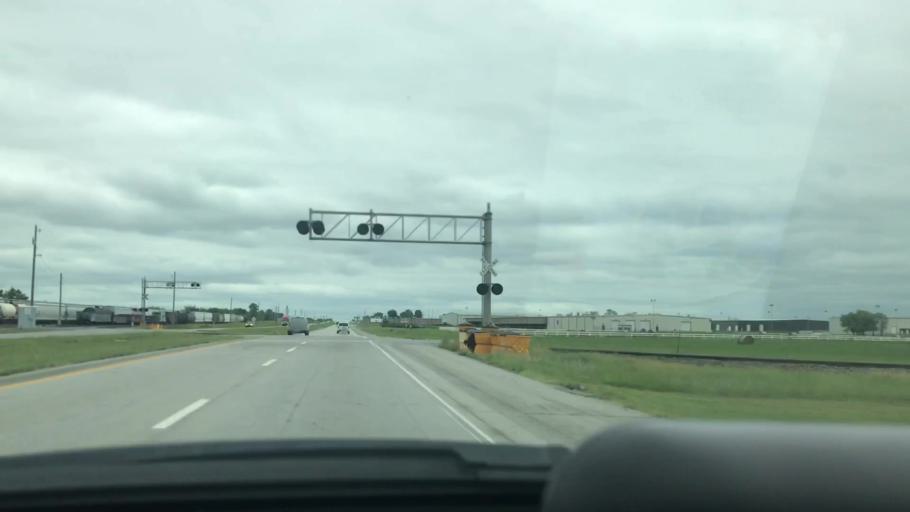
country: US
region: Oklahoma
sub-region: Mayes County
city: Chouteau
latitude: 36.2366
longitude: -95.3382
